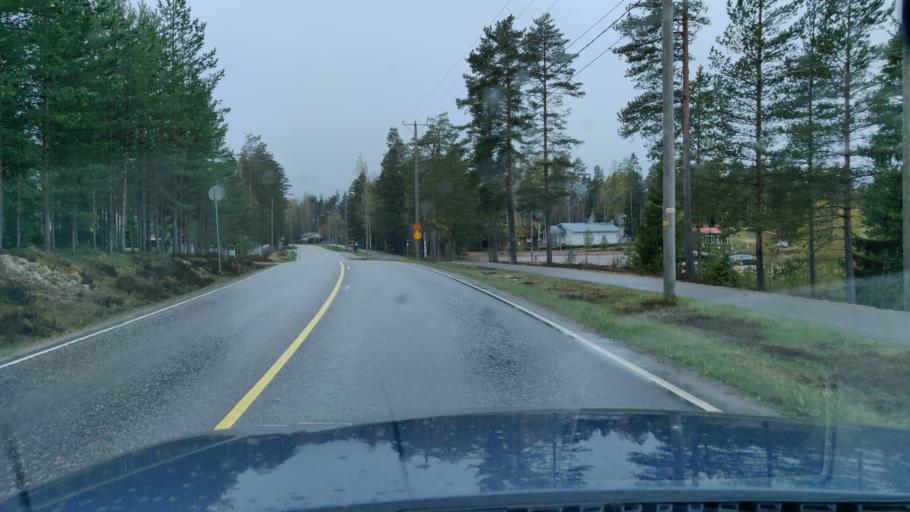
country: FI
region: Uusimaa
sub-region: Helsinki
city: Nurmijaervi
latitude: 60.5222
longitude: 24.7133
